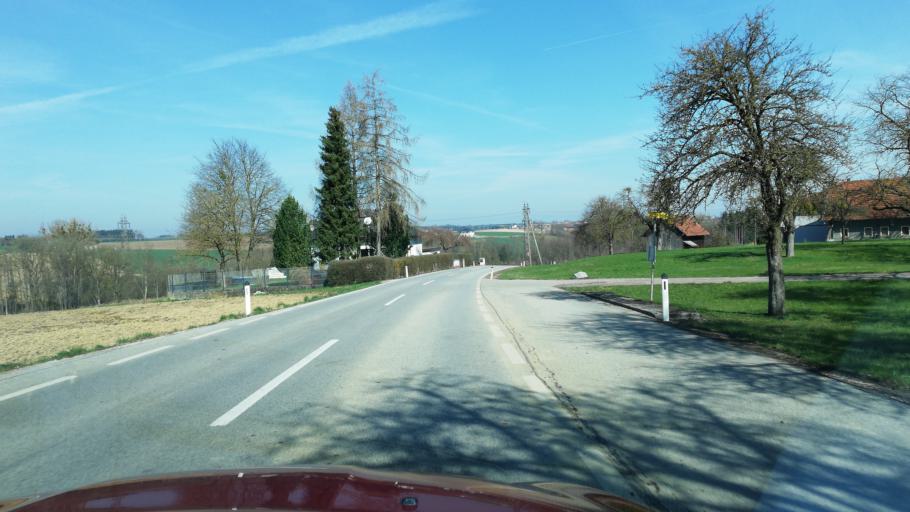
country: AT
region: Upper Austria
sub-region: Politischer Bezirk Kirchdorf an der Krems
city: Kremsmunster
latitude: 48.0876
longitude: 14.1097
